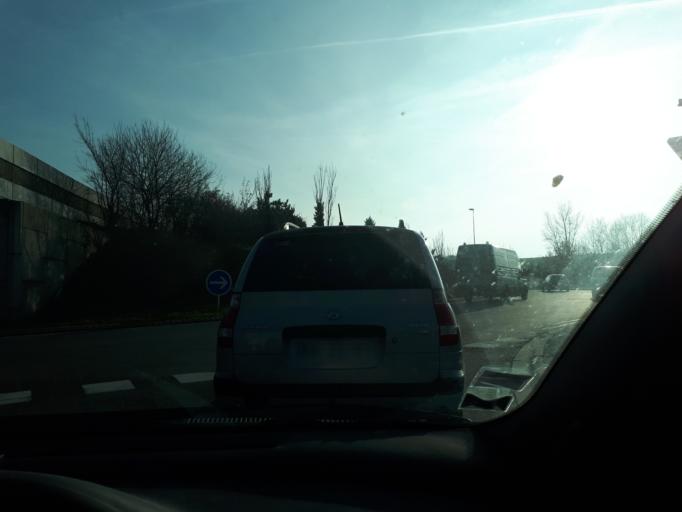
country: FR
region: Alsace
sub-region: Departement du Haut-Rhin
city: Morschwiller-le-Bas
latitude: 47.7375
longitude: 7.2881
